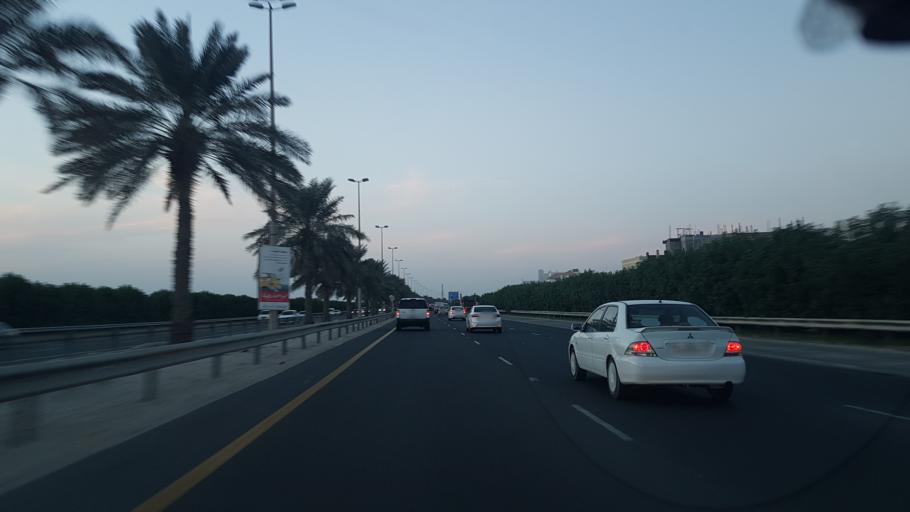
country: BH
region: Central Governorate
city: Madinat Hamad
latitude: 26.1540
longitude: 50.5072
